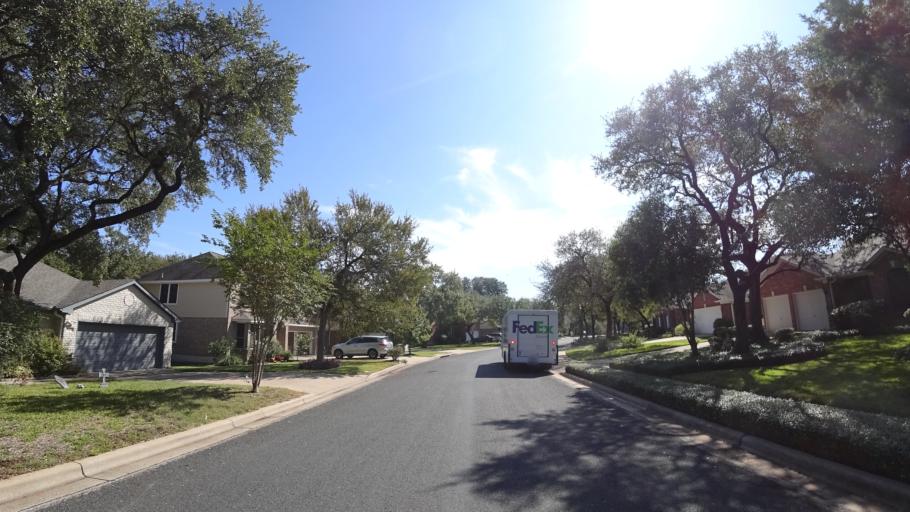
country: US
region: Texas
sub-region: Travis County
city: Shady Hollow
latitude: 30.2109
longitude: -97.8659
